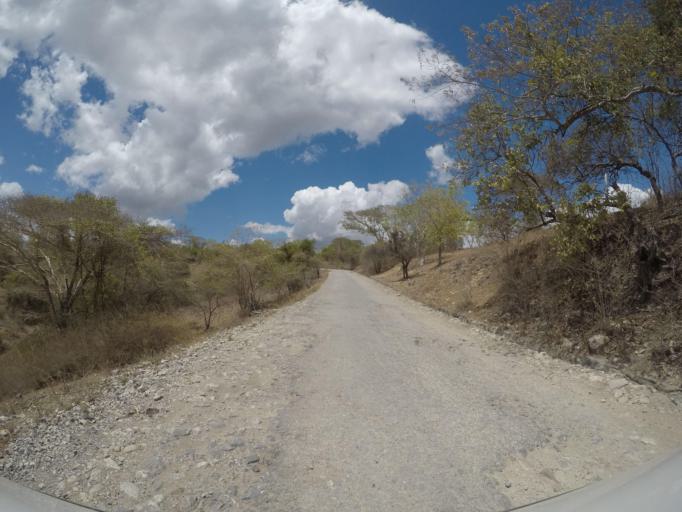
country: TL
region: Baucau
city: Baucau
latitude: -8.4827
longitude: 126.6111
